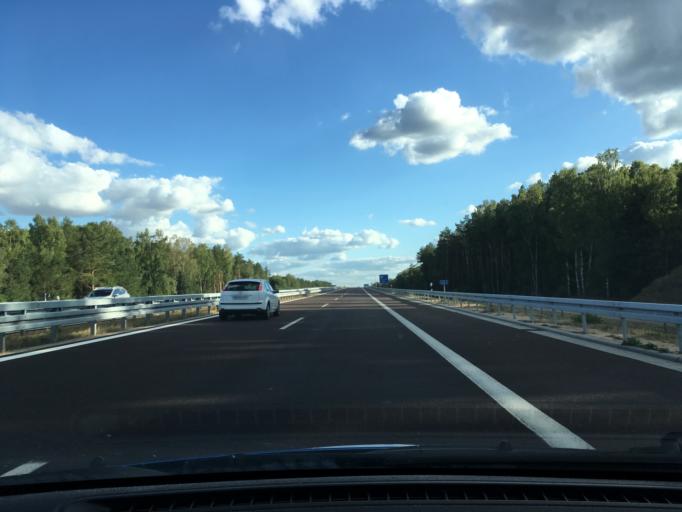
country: DE
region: Mecklenburg-Vorpommern
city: Ludwigslust
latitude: 53.3114
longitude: 11.5276
